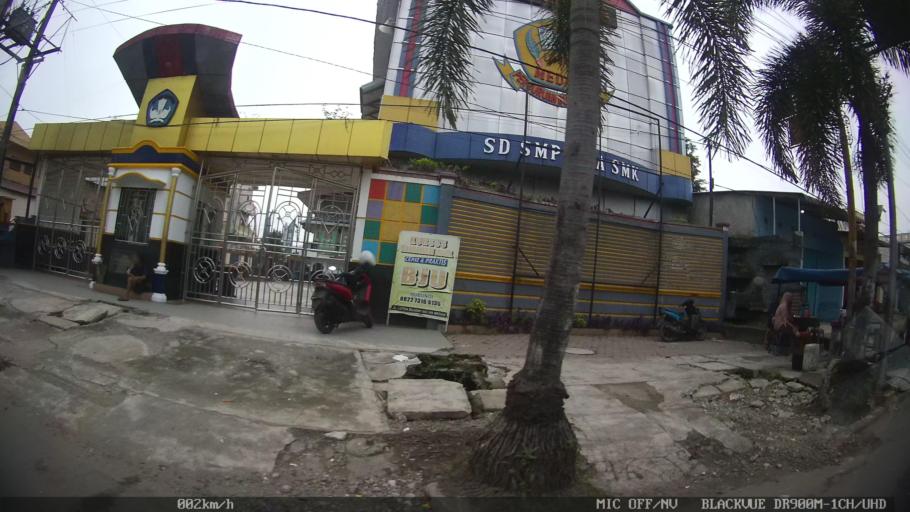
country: ID
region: North Sumatra
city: Medan
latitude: 3.5973
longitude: 98.7222
